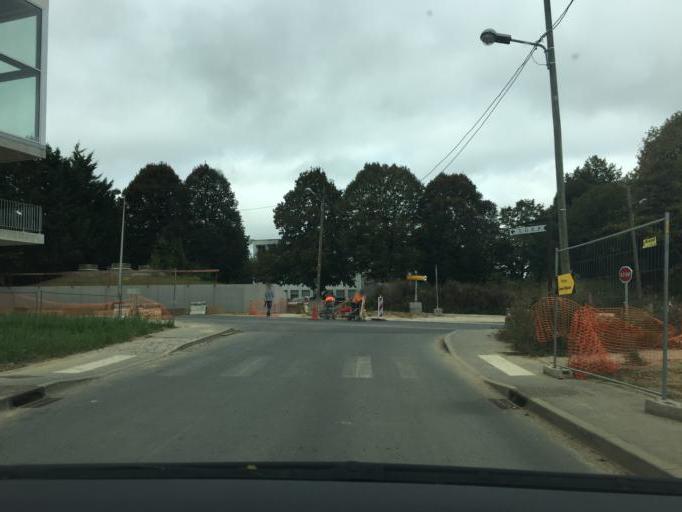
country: FR
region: Ile-de-France
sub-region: Departement de l'Essonne
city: Bures-sur-Yvette
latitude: 48.7094
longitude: 2.1719
